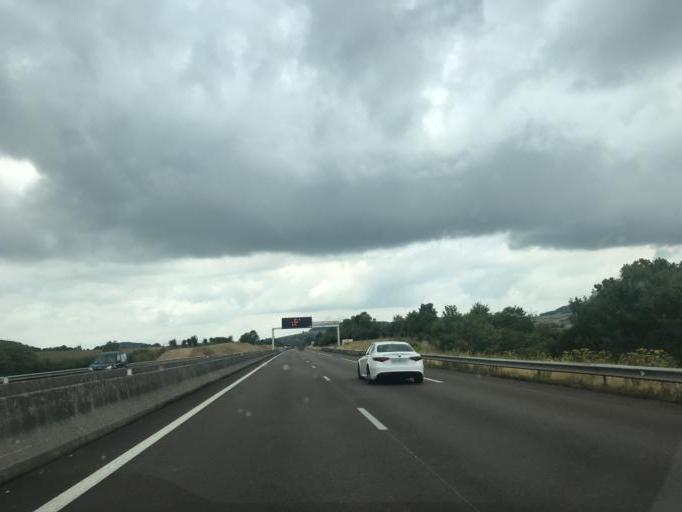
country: FR
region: Bourgogne
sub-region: Departement de la Cote-d'Or
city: Pouilly-en-Auxois
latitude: 47.2329
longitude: 4.5838
